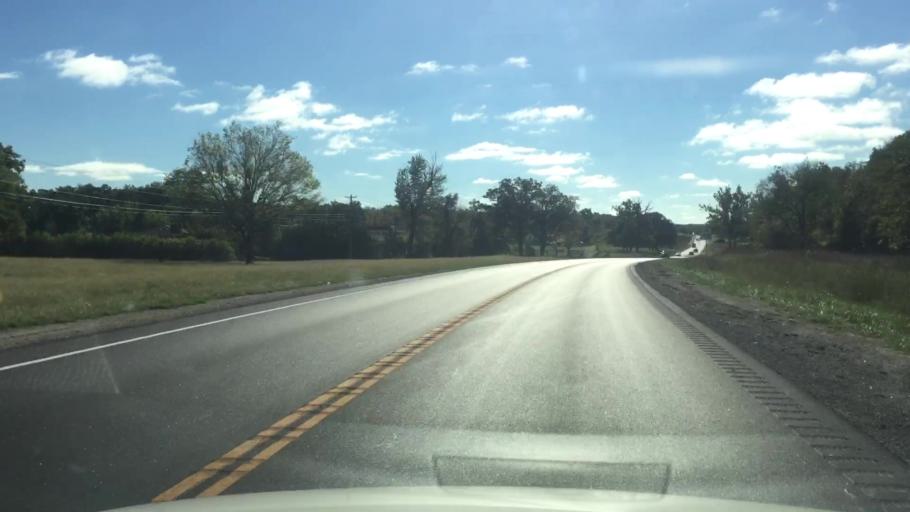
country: US
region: Missouri
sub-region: Boone County
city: Columbia
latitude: 38.9798
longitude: -92.4402
